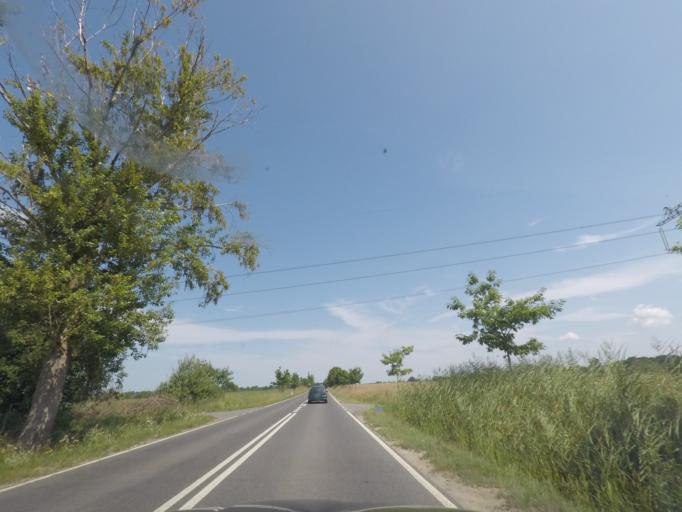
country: PL
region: West Pomeranian Voivodeship
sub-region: Powiat koszalinski
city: Sianow
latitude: 54.2366
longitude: 16.2743
